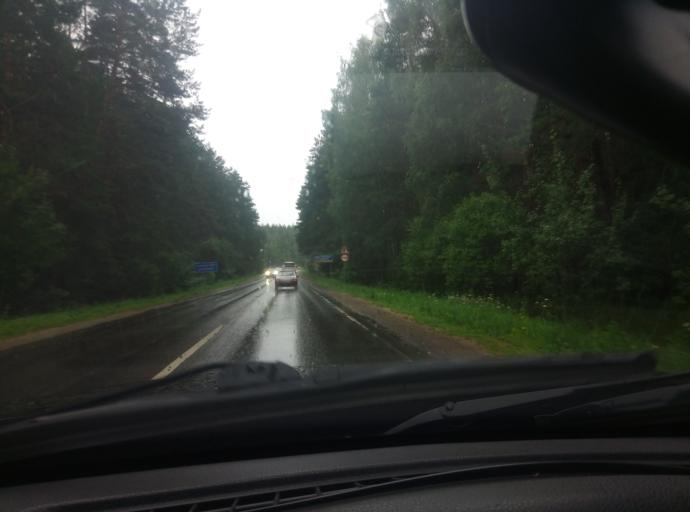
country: RU
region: Kaluga
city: Kremenki
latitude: 54.8817
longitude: 37.1682
